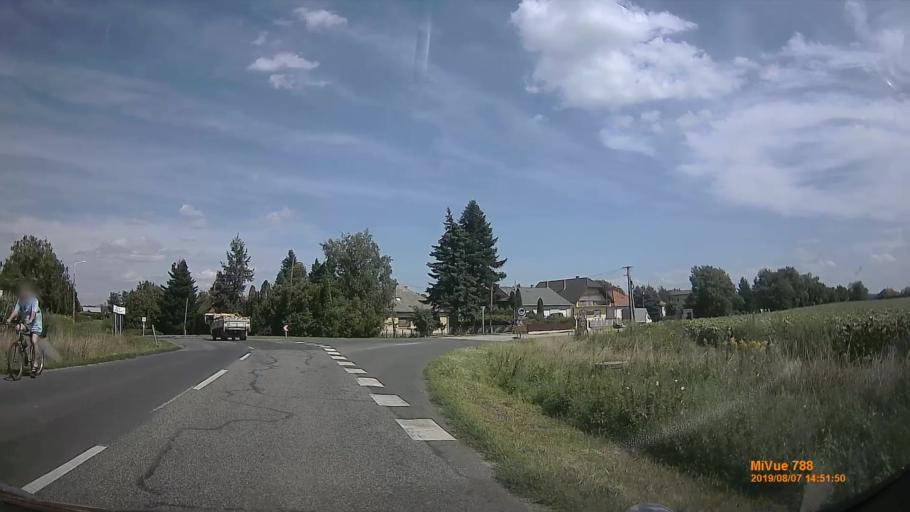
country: HU
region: Zala
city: Zalaegerszeg
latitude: 46.8575
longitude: 16.8426
